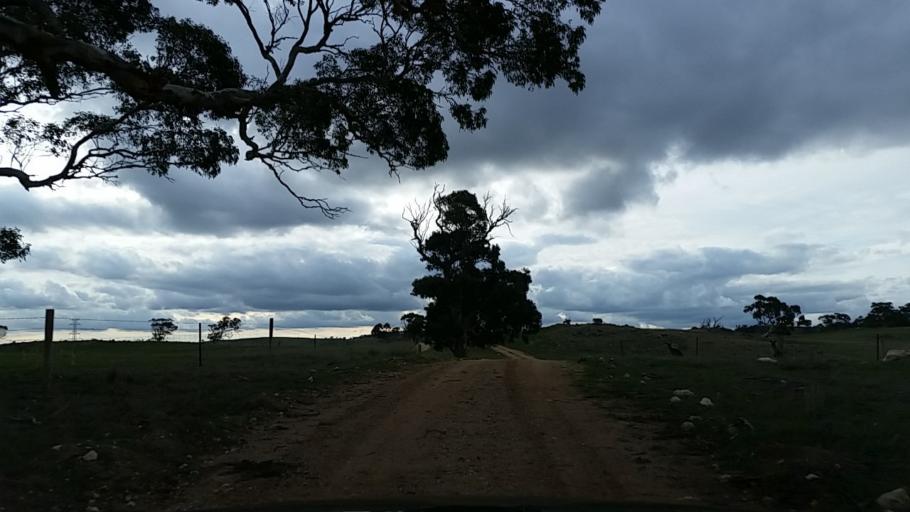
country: AU
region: South Australia
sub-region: Mount Barker
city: Callington
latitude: -34.9631
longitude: 139.0536
